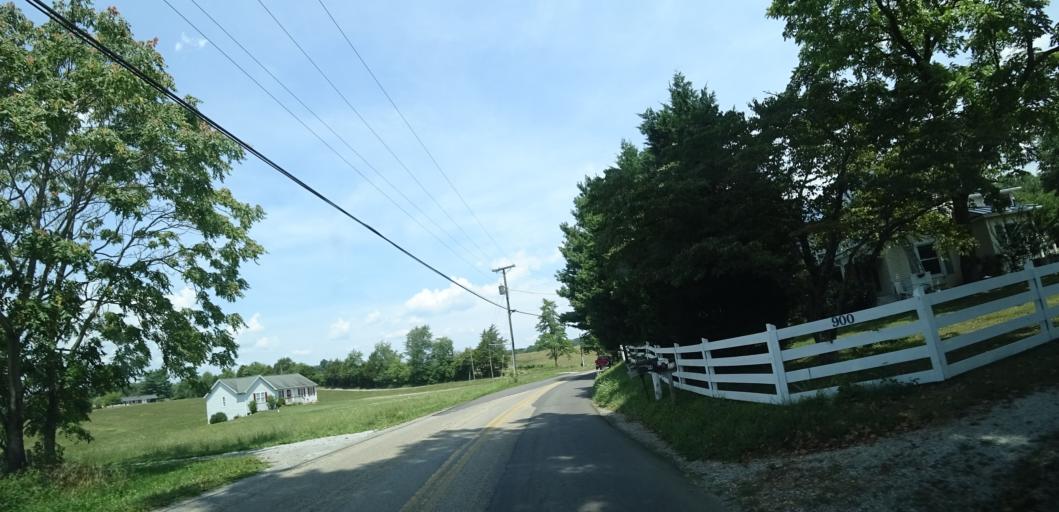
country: US
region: Virginia
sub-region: Botetourt County
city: Fincastle
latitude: 37.4618
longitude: -79.8428
